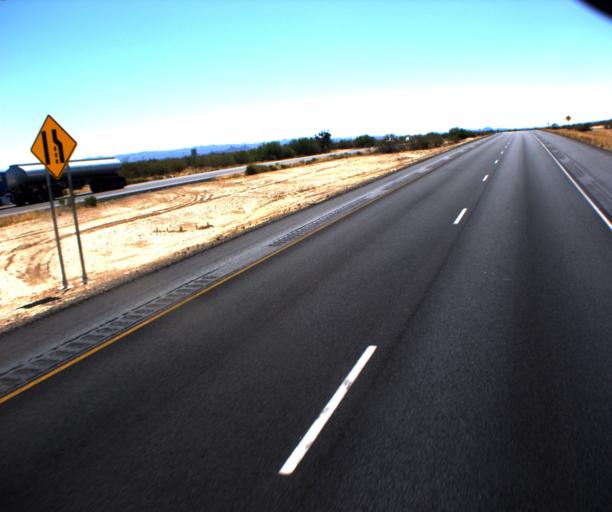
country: US
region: Arizona
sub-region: Yavapai County
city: Congress
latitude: 34.0585
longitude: -112.8579
